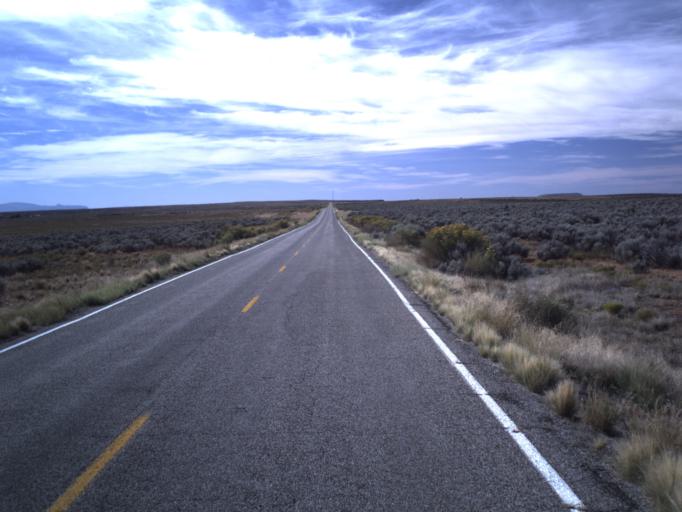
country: US
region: Utah
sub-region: San Juan County
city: Blanding
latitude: 37.3801
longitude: -109.3415
